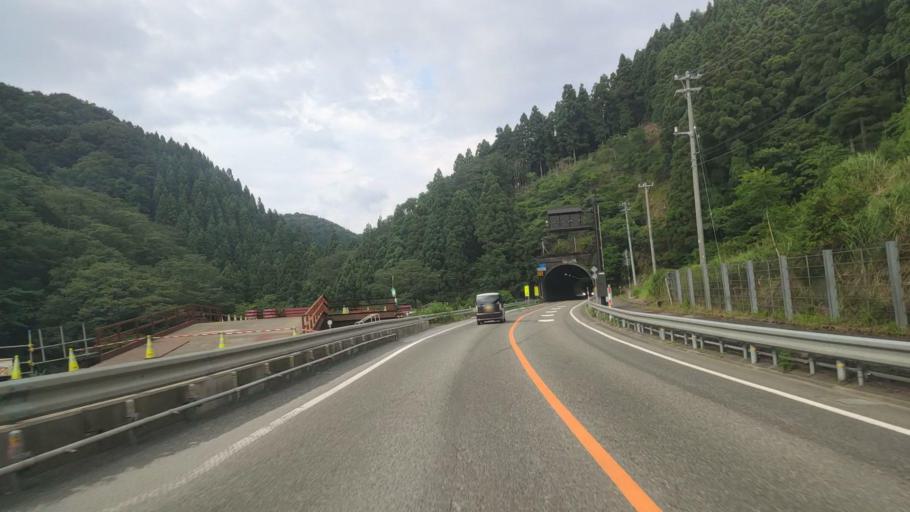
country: JP
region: Fukui
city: Takefu
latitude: 35.8235
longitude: 136.1043
